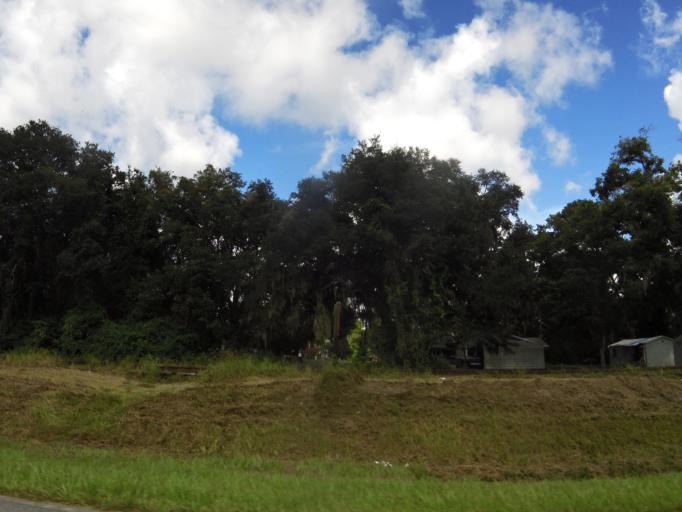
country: US
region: Georgia
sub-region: Camden County
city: Kingsland
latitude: 30.8055
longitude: -81.6926
